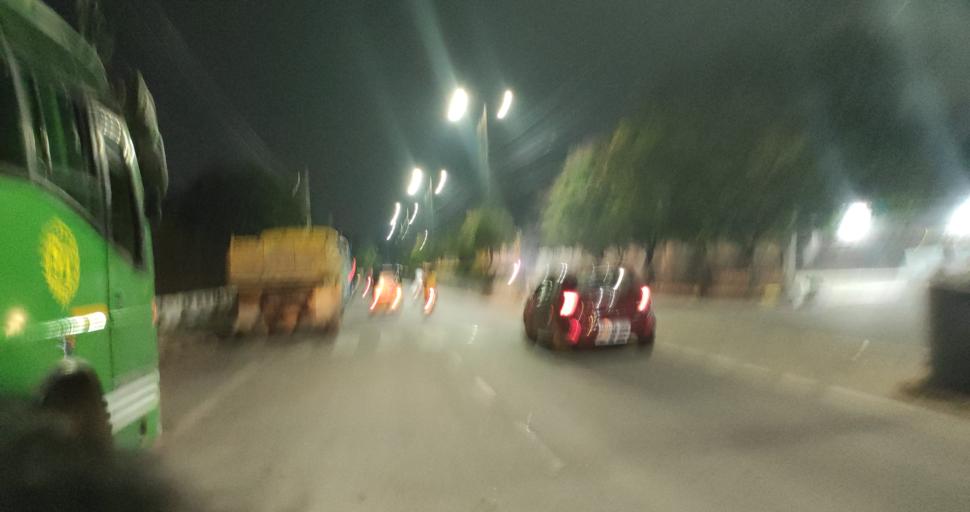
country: IN
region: Telangana
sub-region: Rangareddi
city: Gaddi Annaram
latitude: 17.3642
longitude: 78.4997
